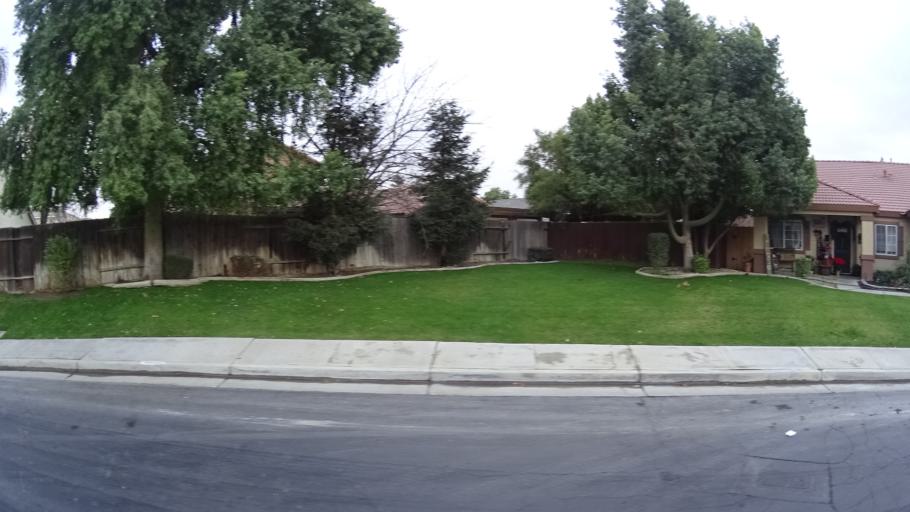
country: US
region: California
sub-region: Kern County
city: Greenfield
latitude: 35.2982
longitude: -119.0773
